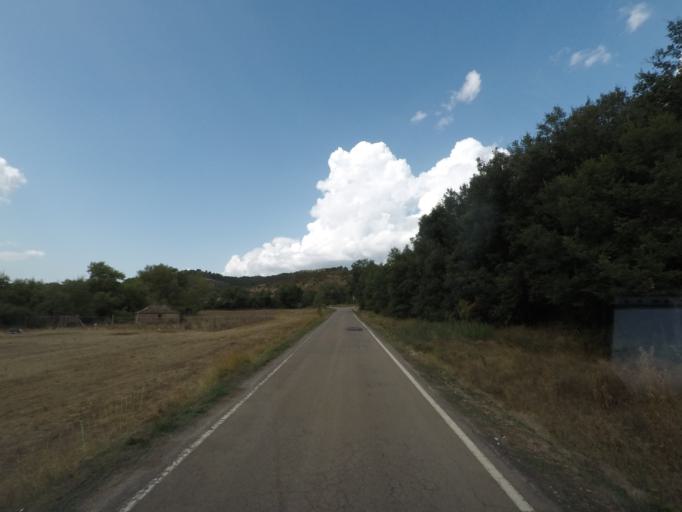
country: ES
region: Aragon
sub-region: Provincia de Huesca
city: Yebra de Basa
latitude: 42.3925
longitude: -0.2886
